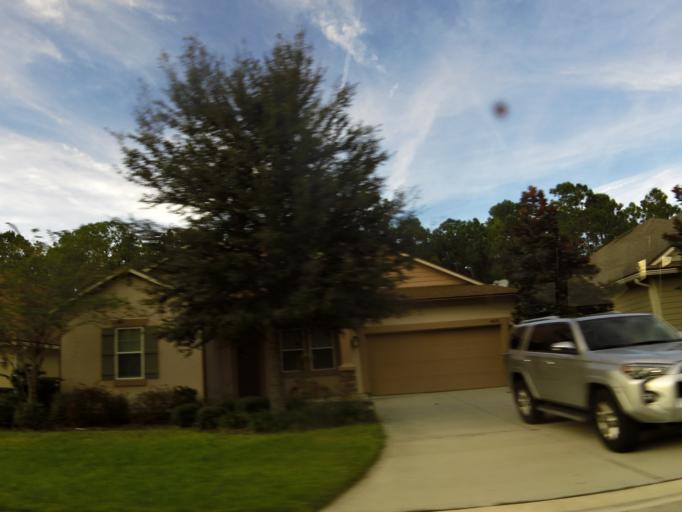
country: US
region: Florida
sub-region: Saint Johns County
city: Fruit Cove
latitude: 30.1497
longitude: -81.5395
